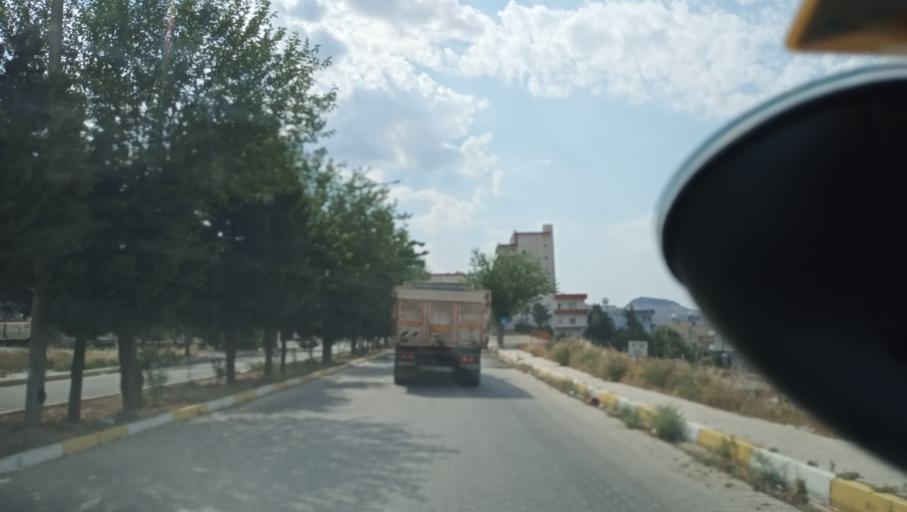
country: TR
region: Mardin
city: Kabala
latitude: 37.3417
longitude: 40.8096
